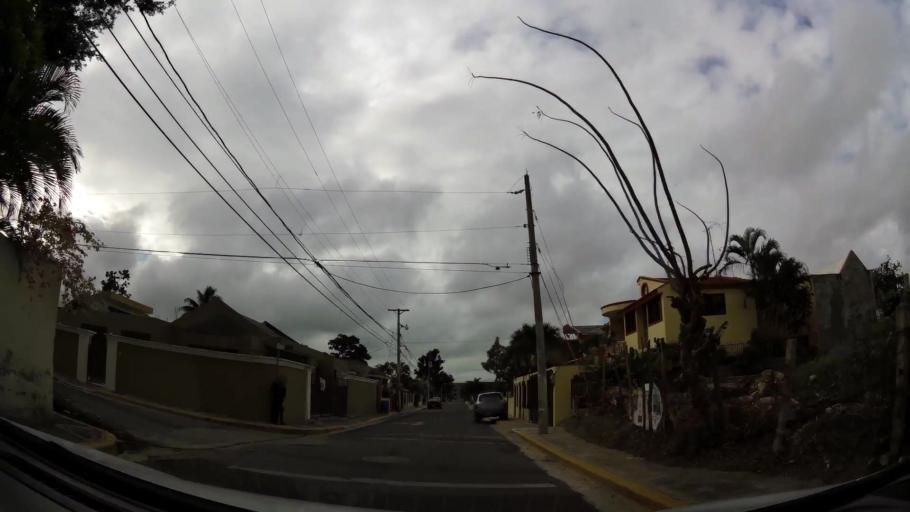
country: DO
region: Santiago
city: Santiago de los Caballeros
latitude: 19.4656
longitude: -70.6553
